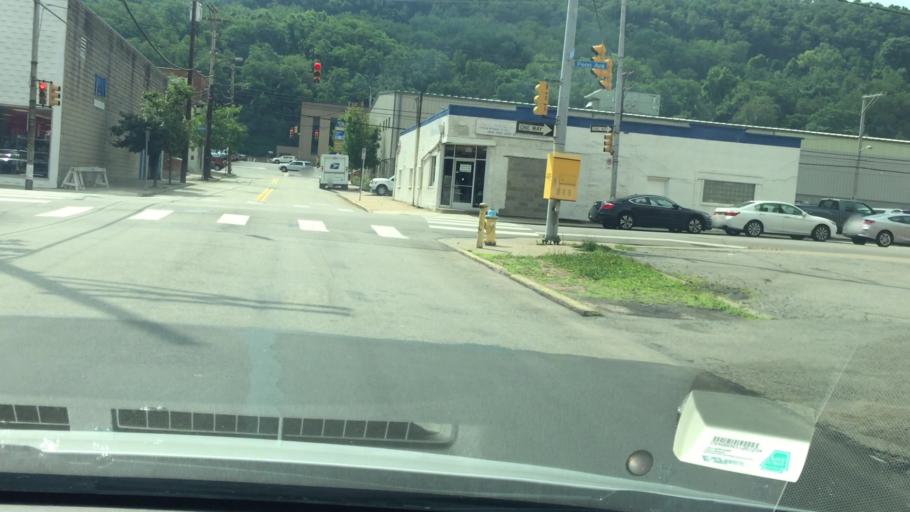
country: US
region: Pennsylvania
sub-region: Allegheny County
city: Millvale
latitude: 40.4570
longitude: -79.9759
